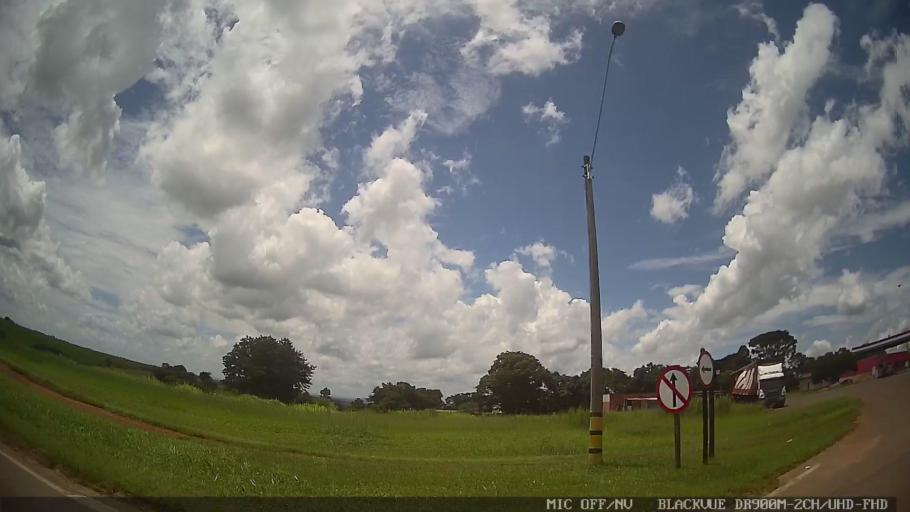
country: BR
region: Sao Paulo
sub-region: Laranjal Paulista
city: Laranjal Paulista
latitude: -23.0377
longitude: -47.8647
